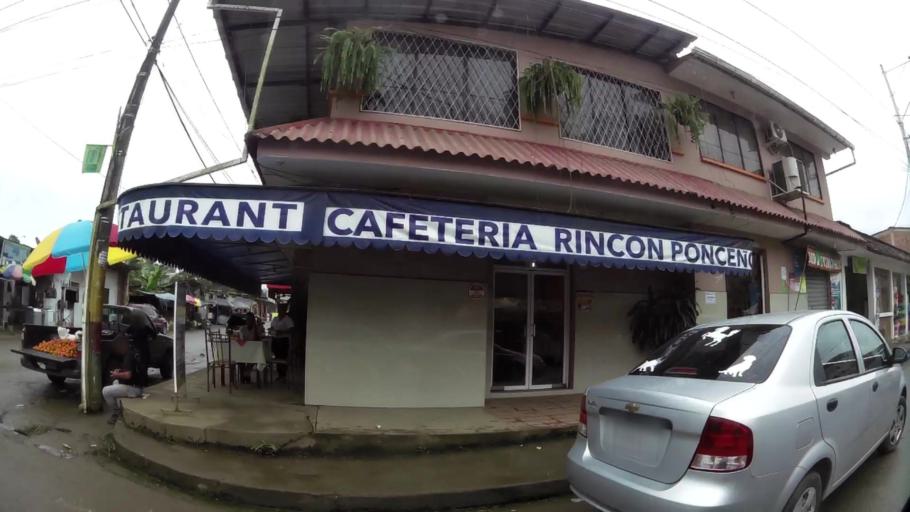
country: EC
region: Guayas
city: Balao
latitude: -3.0606
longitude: -79.7459
